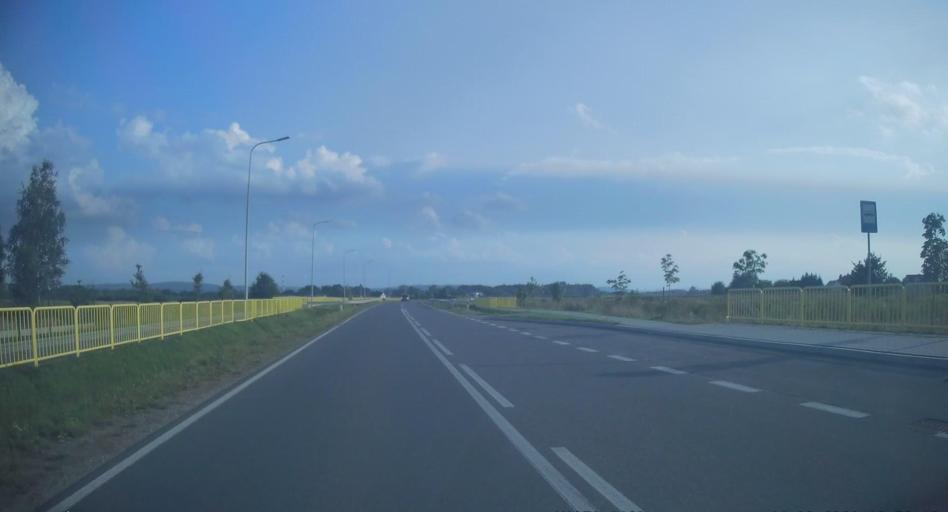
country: PL
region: Subcarpathian Voivodeship
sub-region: Powiat debicki
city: Zyrakow
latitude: 50.0714
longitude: 21.3807
